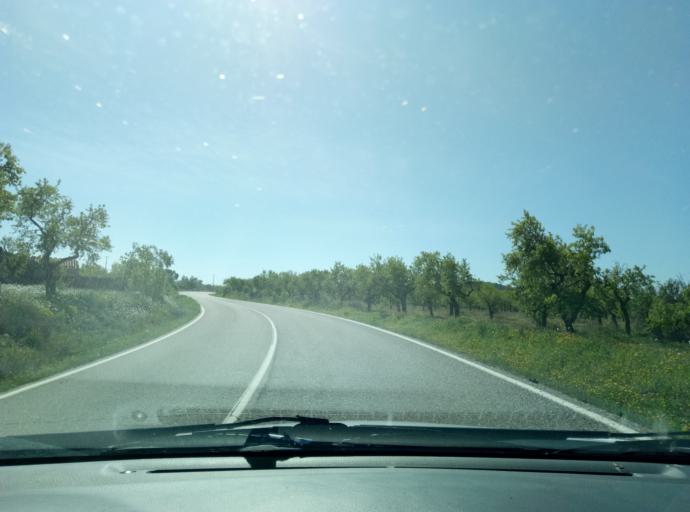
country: ES
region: Catalonia
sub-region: Provincia de Lleida
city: Vallbona de les Monges
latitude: 41.5460
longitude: 1.0268
